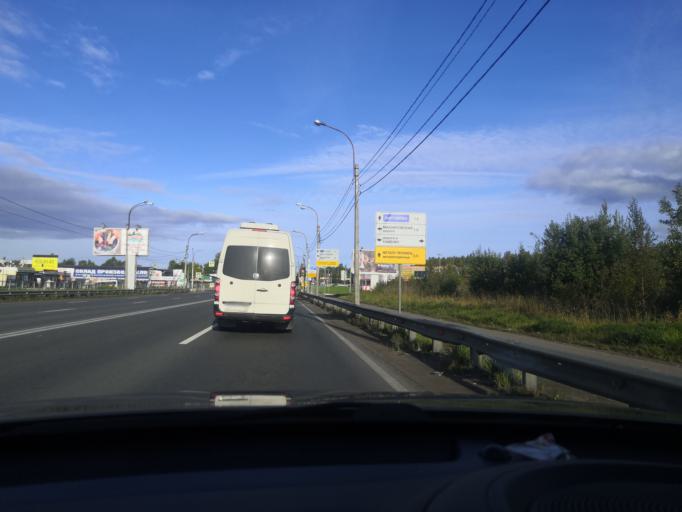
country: RU
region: St.-Petersburg
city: Pargolovo
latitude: 60.0715
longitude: 30.2864
